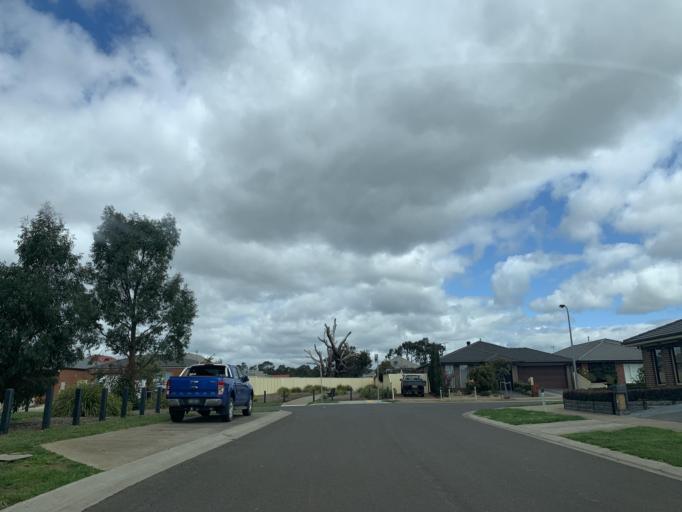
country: AU
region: Victoria
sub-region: Whittlesea
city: Whittlesea
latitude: -37.2906
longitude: 144.9330
